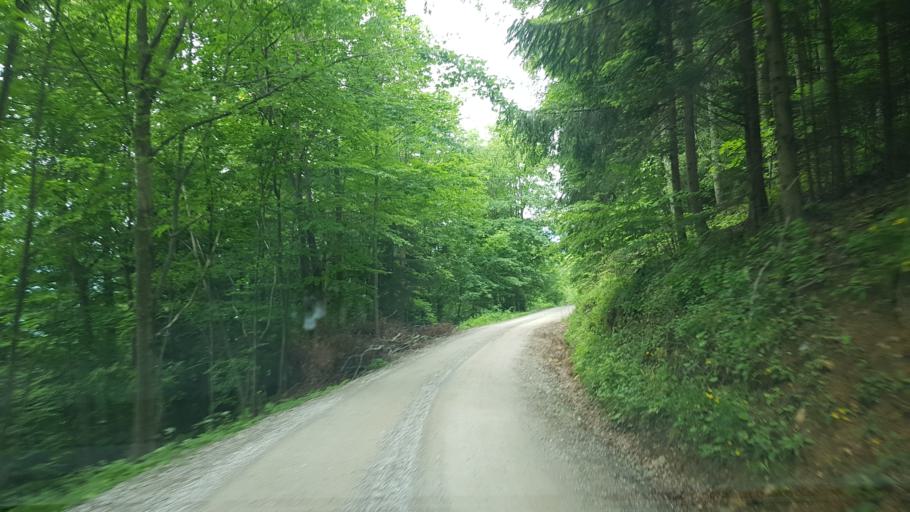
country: SI
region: Dobrna
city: Dobrna
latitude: 46.3616
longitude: 15.2473
